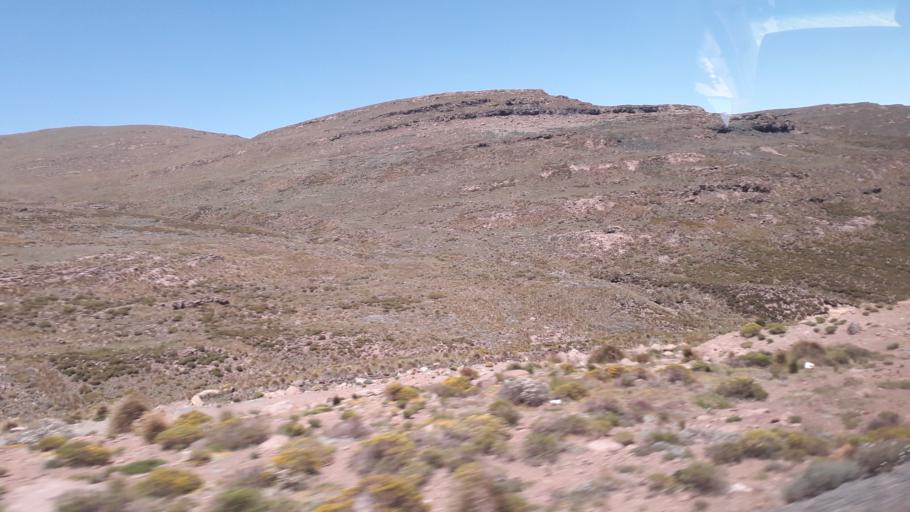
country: ZA
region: Orange Free State
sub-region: Thabo Mofutsanyana District Municipality
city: Phuthaditjhaba
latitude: -28.8066
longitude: 28.6995
